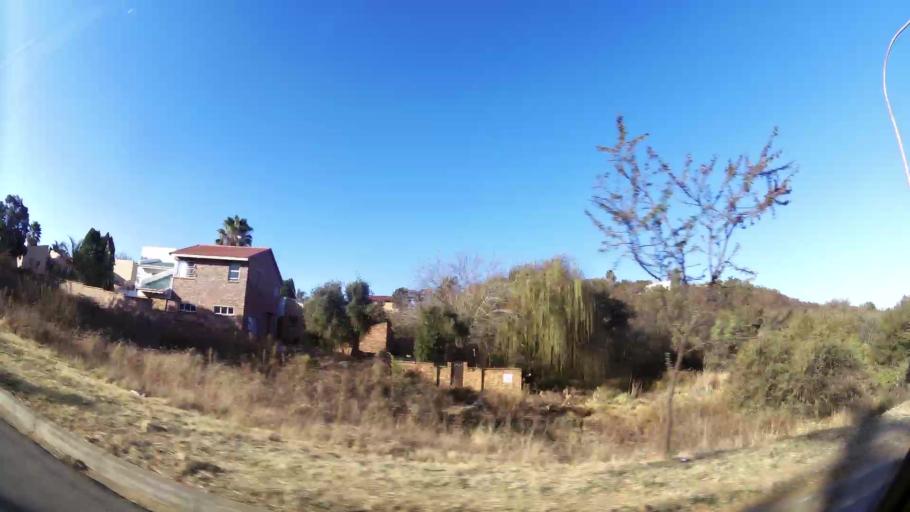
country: ZA
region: Gauteng
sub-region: City of Johannesburg Metropolitan Municipality
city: Johannesburg
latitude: -26.2878
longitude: 28.0713
